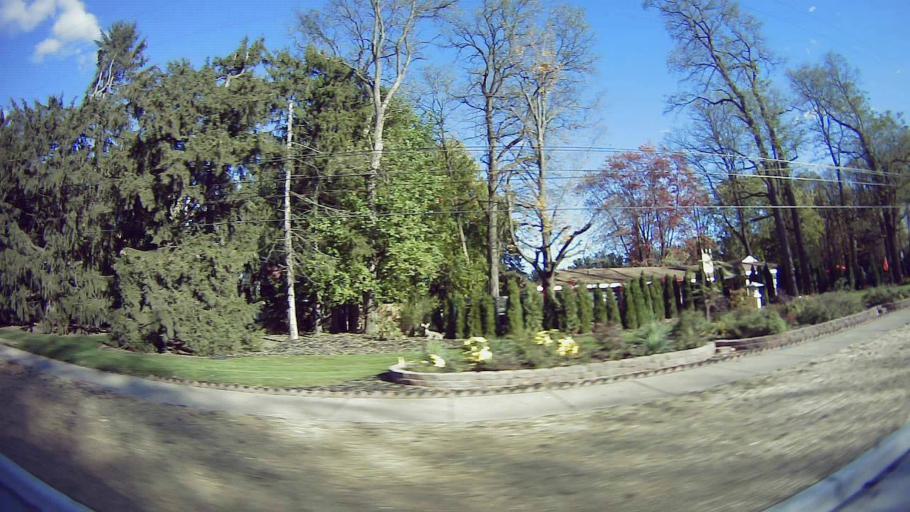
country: US
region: Michigan
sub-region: Oakland County
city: Southfield
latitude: 42.4620
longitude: -83.2400
